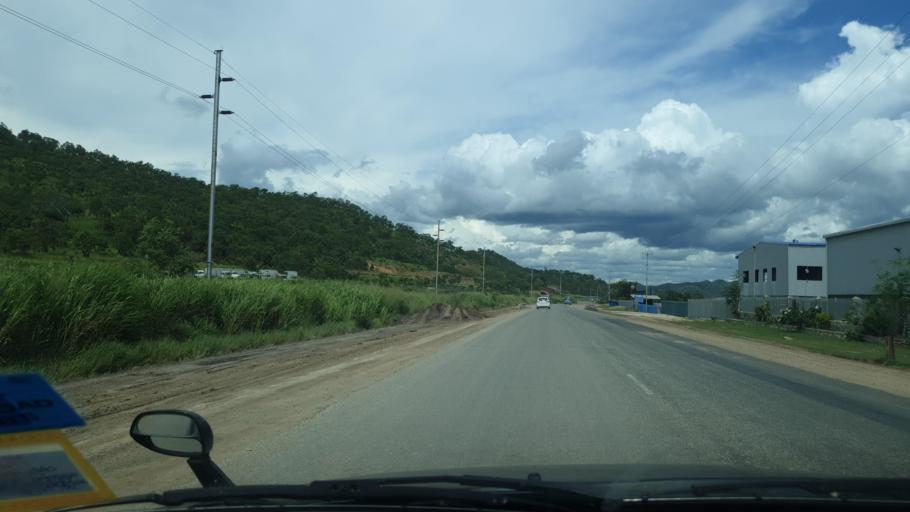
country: PG
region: National Capital
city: Port Moresby
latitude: -9.4198
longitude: 147.0821
